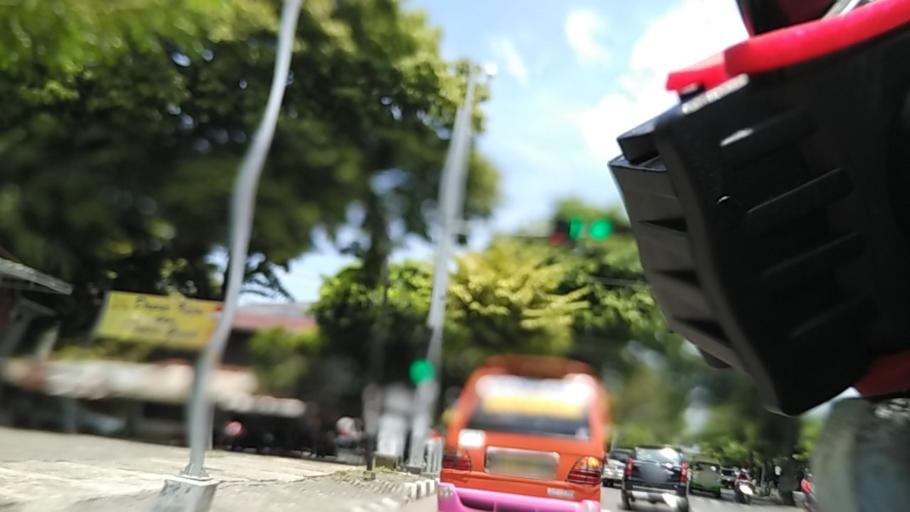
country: ID
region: Central Java
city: Semarang
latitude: -6.9876
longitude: 110.3827
